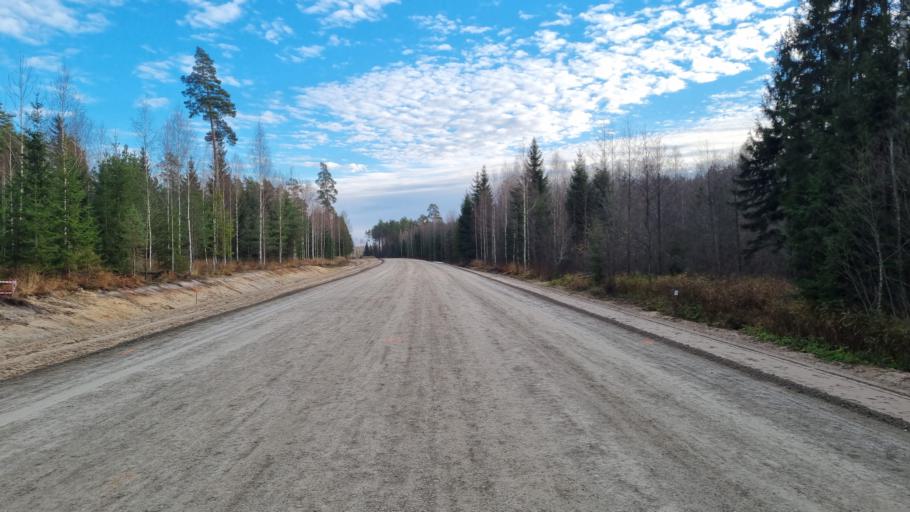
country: LV
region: Kekava
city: Kekava
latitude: 56.7914
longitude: 24.2148
